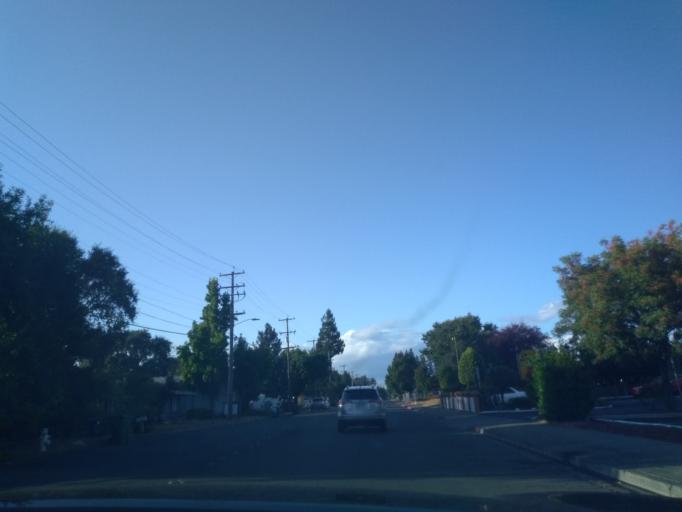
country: US
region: California
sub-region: Mendocino County
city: Ukiah
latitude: 39.1449
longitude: -123.1984
